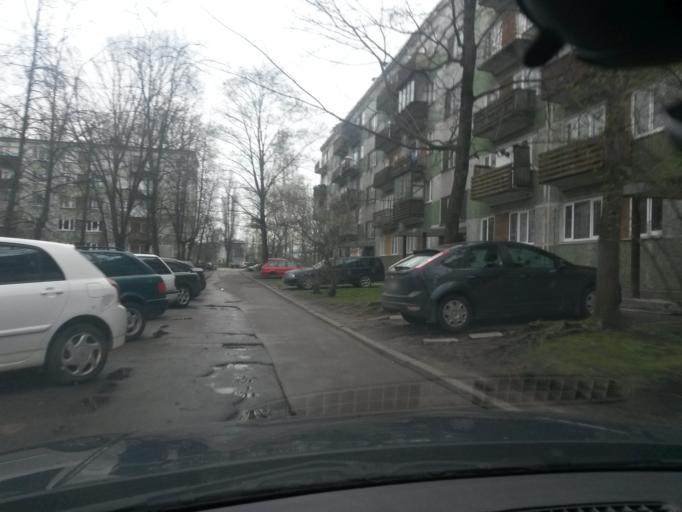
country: LV
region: Kekava
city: Balozi
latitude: 56.9178
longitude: 24.1840
